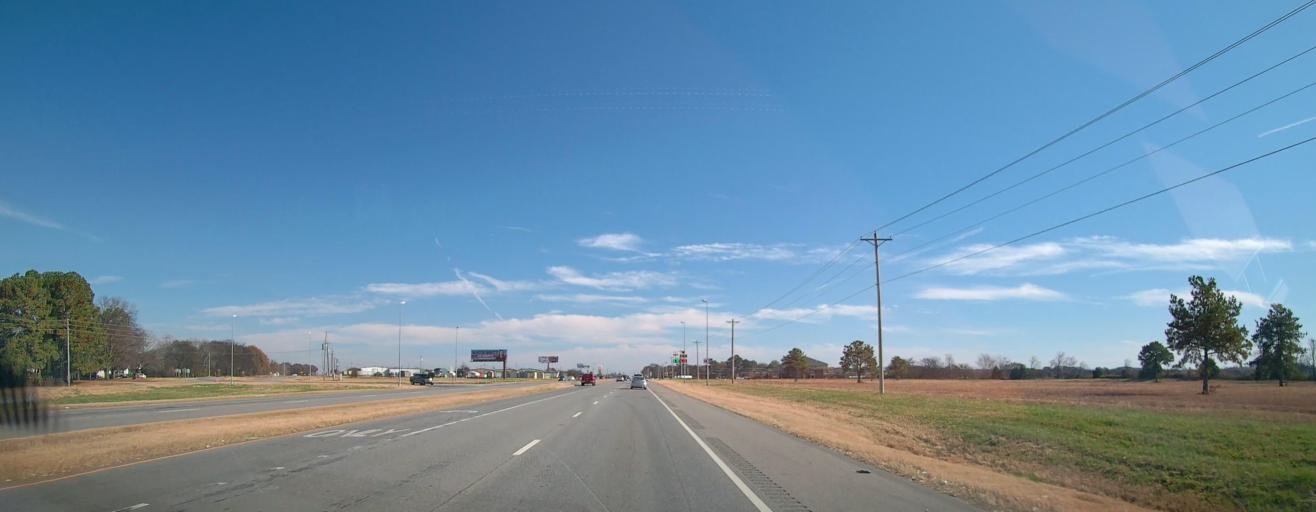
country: US
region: Alabama
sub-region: Colbert County
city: Muscle Shoals
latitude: 34.7004
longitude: -87.6420
